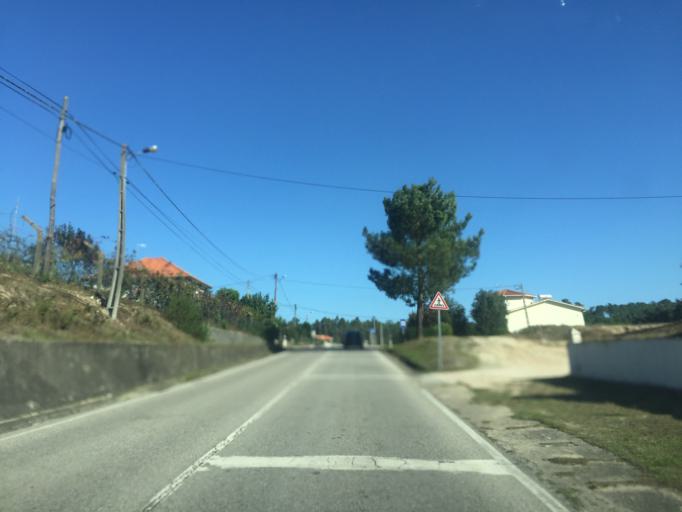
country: PT
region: Leiria
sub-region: Leiria
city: Monte Redondo
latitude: 39.9106
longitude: -8.8214
